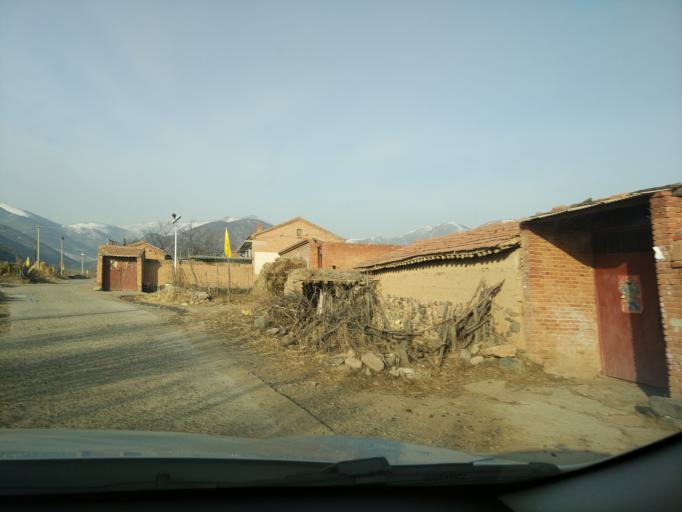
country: CN
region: Hebei
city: Xiwanzi
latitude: 40.8487
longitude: 115.5082
